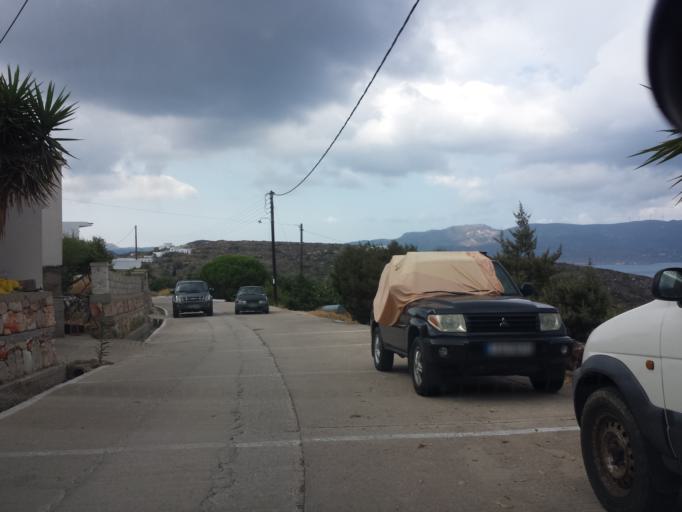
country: GR
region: South Aegean
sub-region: Nomos Kykladon
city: Milos
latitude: 36.7389
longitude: 24.4242
